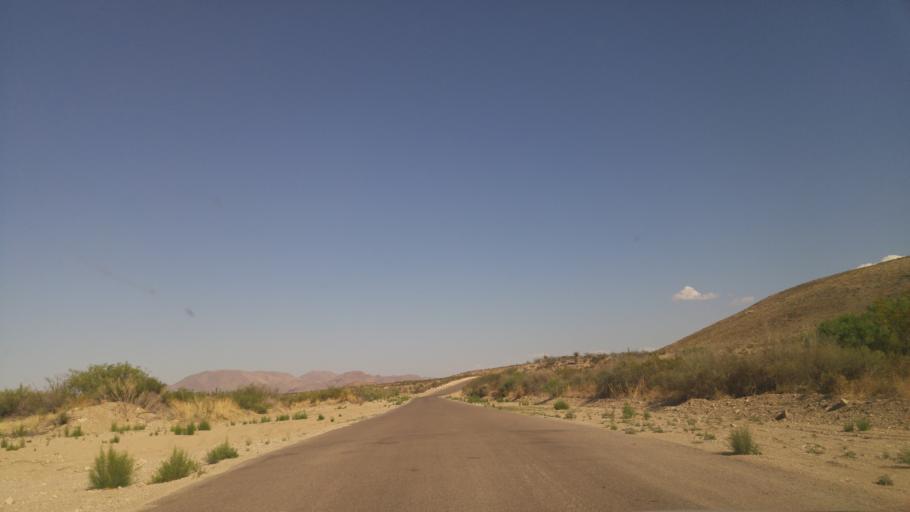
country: US
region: Texas
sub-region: Brewster County
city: Alpine
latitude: 29.5310
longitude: -103.4183
